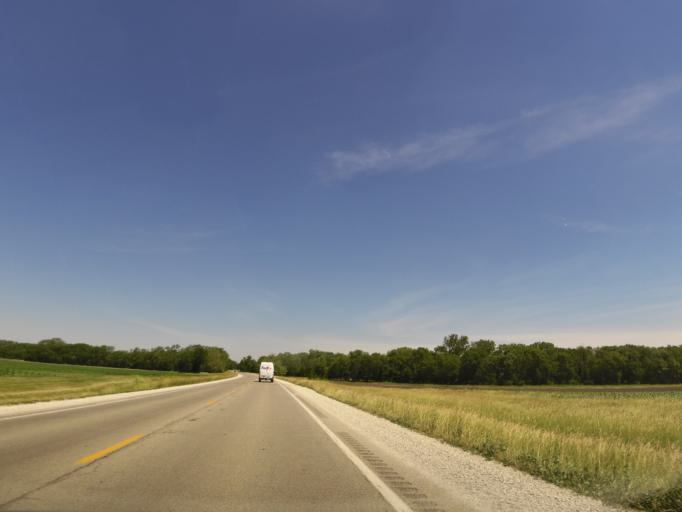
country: US
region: Illinois
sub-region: Vermilion County
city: Rossville
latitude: 40.3259
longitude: -87.6596
